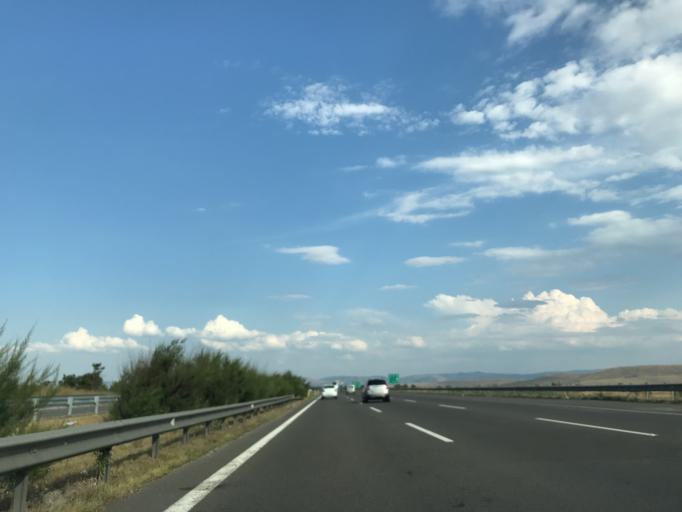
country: TR
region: Bolu
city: Dortdivan
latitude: 40.7411
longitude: 32.1287
